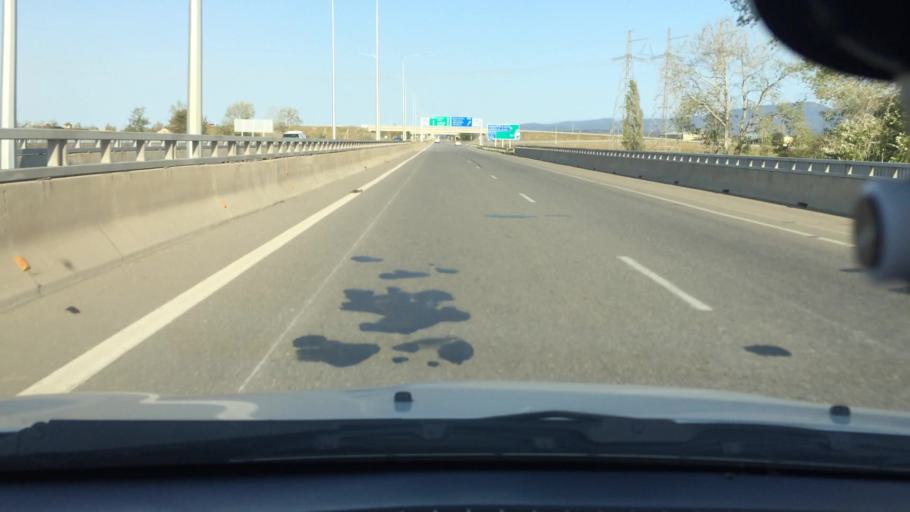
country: GE
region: Imereti
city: Zestap'oni
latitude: 42.1561
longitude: 42.9545
